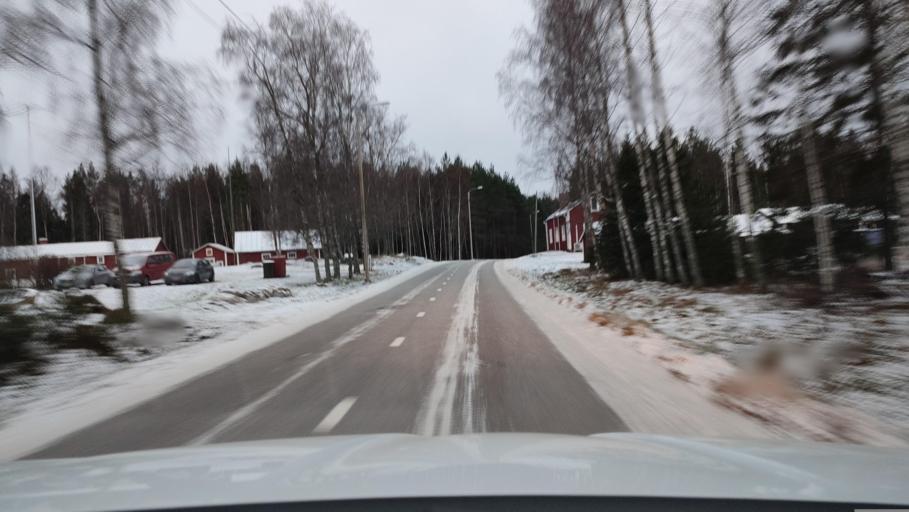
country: FI
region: Ostrobothnia
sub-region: Vaasa
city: Replot
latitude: 63.3544
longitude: 21.3029
